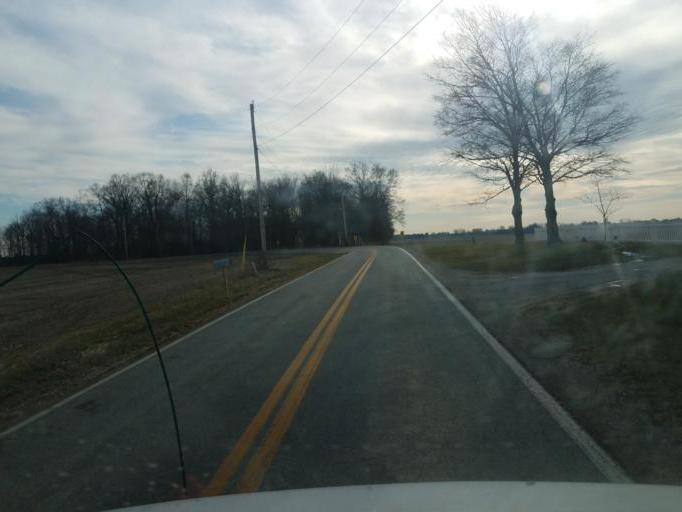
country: US
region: Ohio
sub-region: Delaware County
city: Ashley
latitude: 40.3458
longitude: -82.9664
